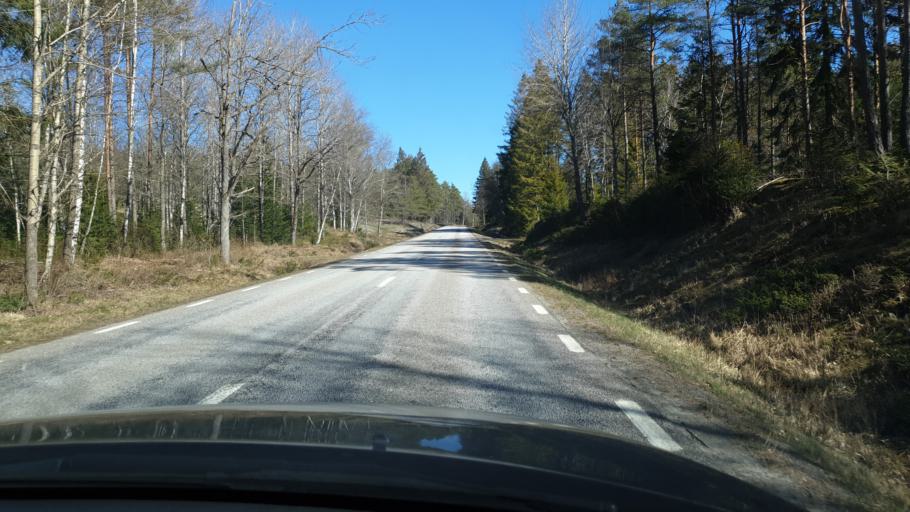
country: SE
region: Vaestra Goetaland
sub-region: Tanums Kommun
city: Tanumshede
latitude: 58.7402
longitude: 11.4521
